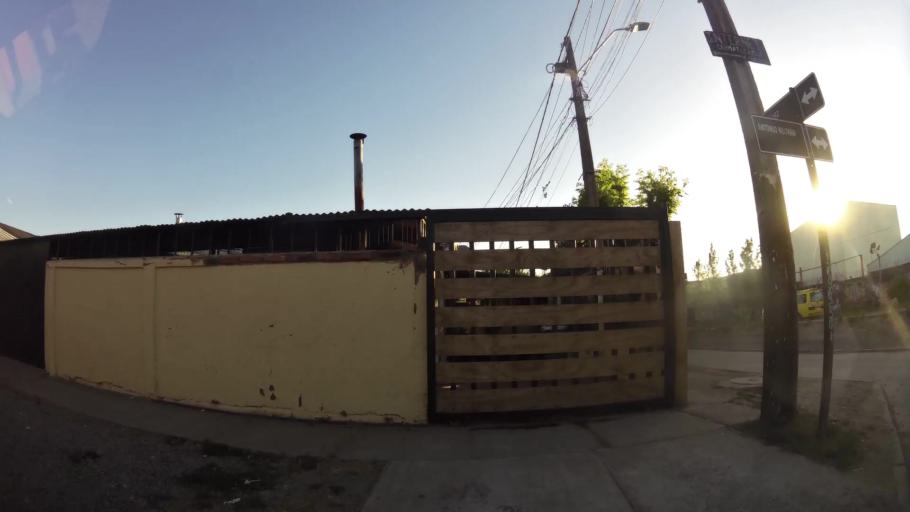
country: CL
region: Santiago Metropolitan
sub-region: Provincia de Maipo
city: San Bernardo
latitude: -33.5810
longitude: -70.6935
